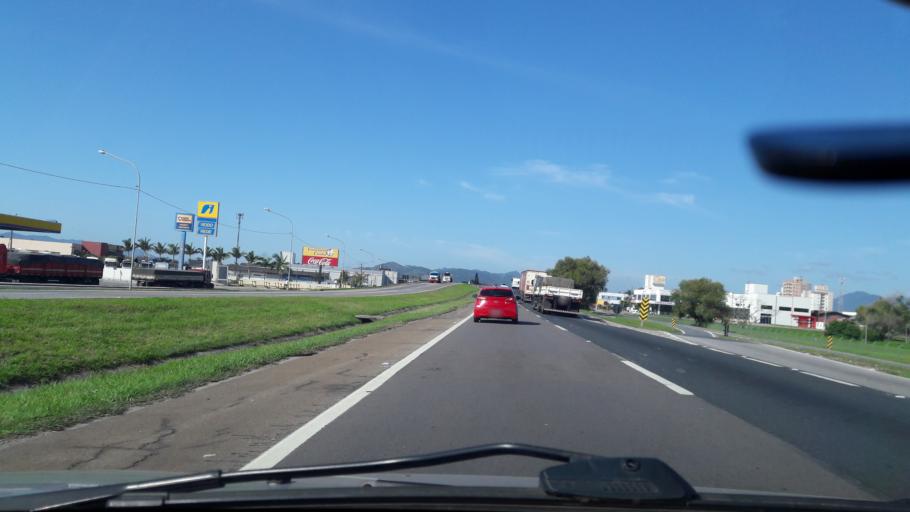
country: BR
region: Santa Catarina
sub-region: Tijucas
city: Tijucas
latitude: -27.2286
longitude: -48.6289
